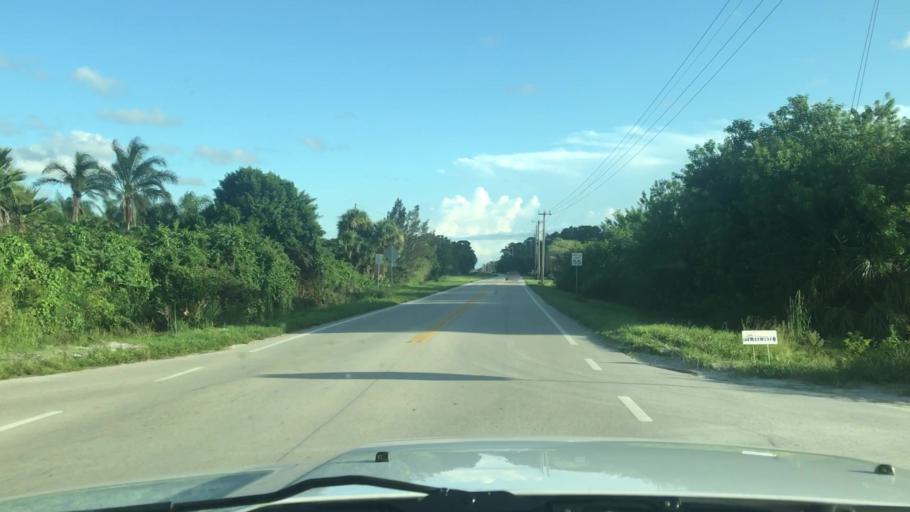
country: US
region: Florida
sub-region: Indian River County
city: Winter Beach
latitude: 27.7338
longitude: -80.4622
